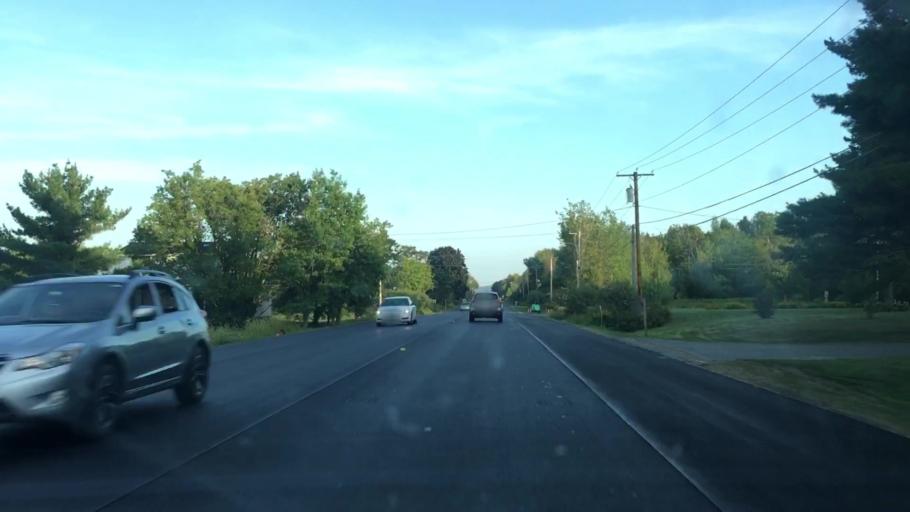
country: US
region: Maine
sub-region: Penobscot County
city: Hampden
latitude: 44.7614
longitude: -68.8484
